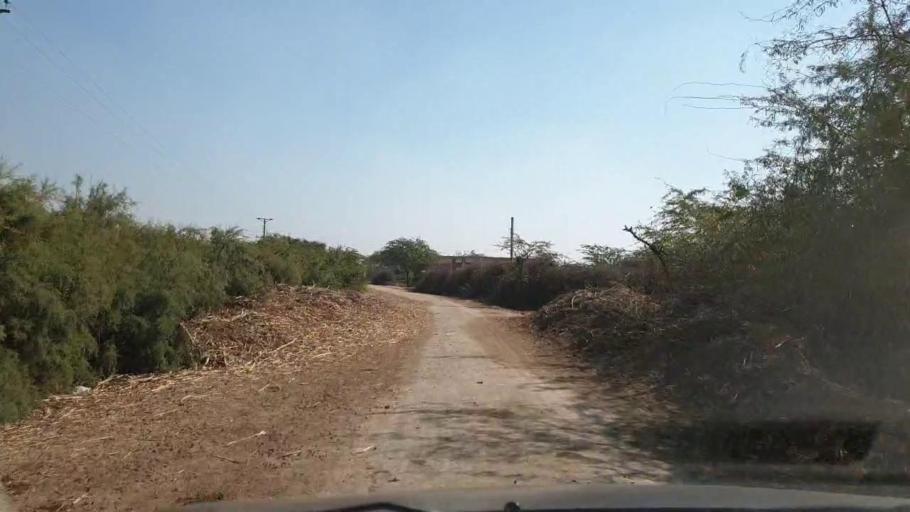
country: PK
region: Sindh
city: Jhol
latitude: 25.9040
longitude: 68.7936
